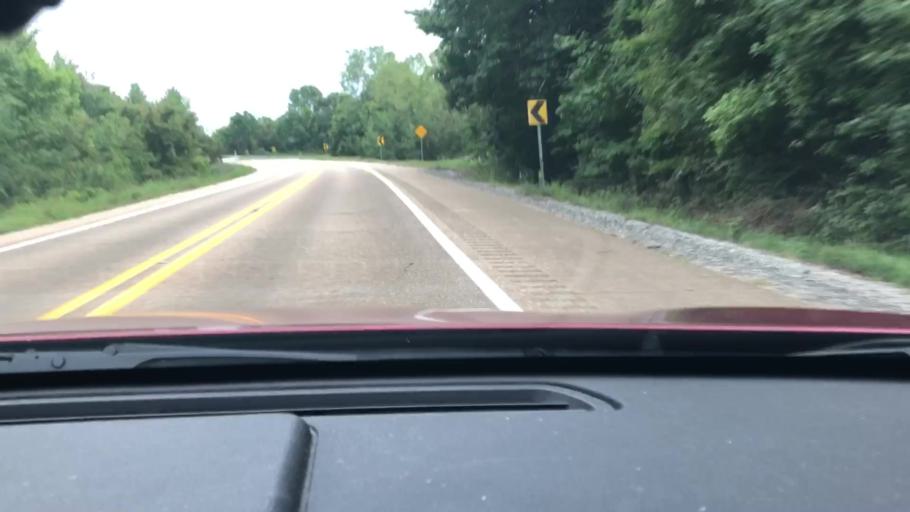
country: US
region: Arkansas
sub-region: Miller County
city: Texarkana
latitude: 33.4146
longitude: -93.8100
